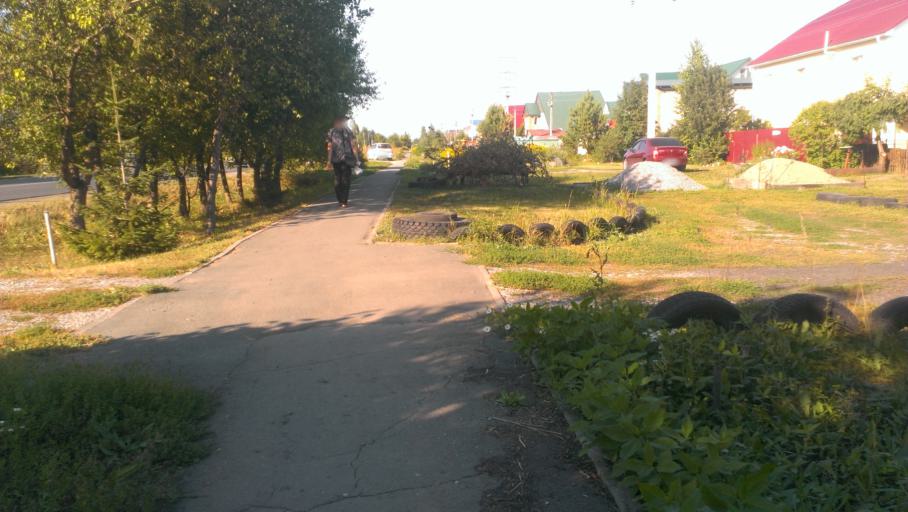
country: RU
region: Altai Krai
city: Novosilikatnyy
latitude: 53.3539
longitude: 83.6341
